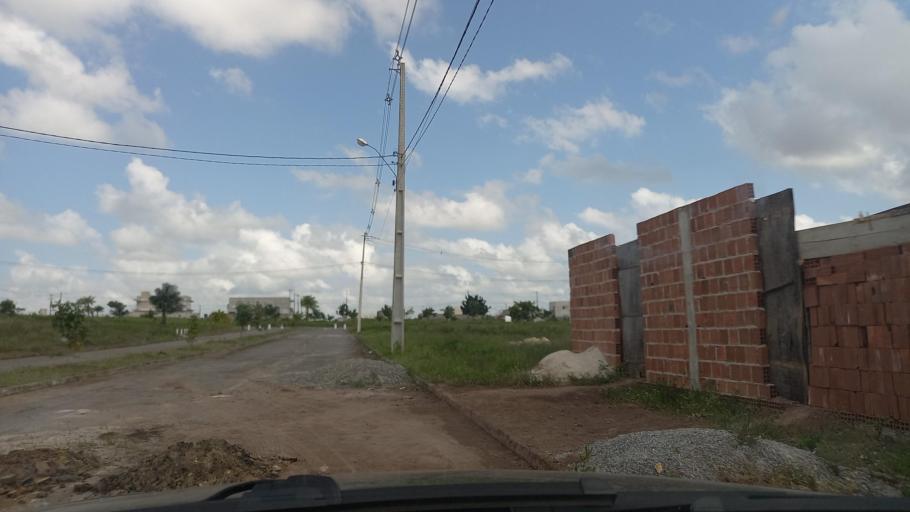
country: BR
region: Pernambuco
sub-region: Goiana
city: Goiana
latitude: -7.5664
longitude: -35.0323
